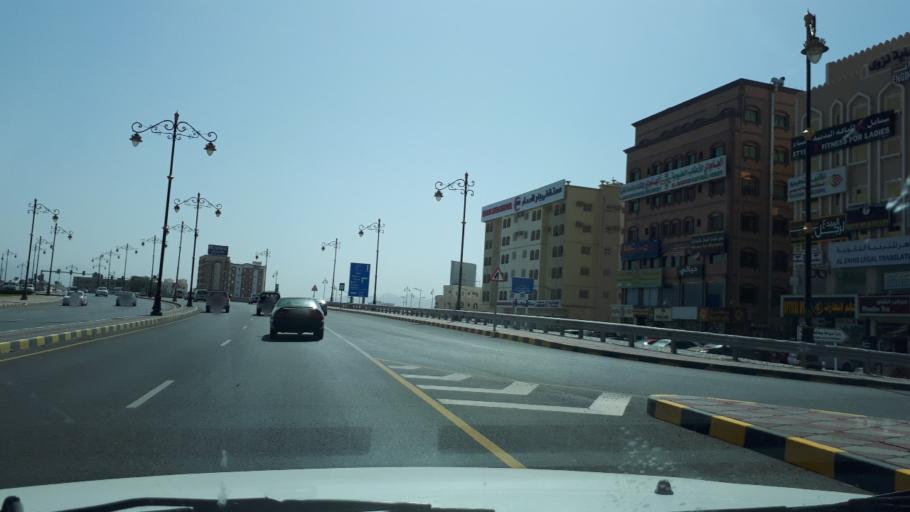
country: OM
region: Muhafazat ad Dakhiliyah
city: Nizwa
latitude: 22.8747
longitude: 57.5313
